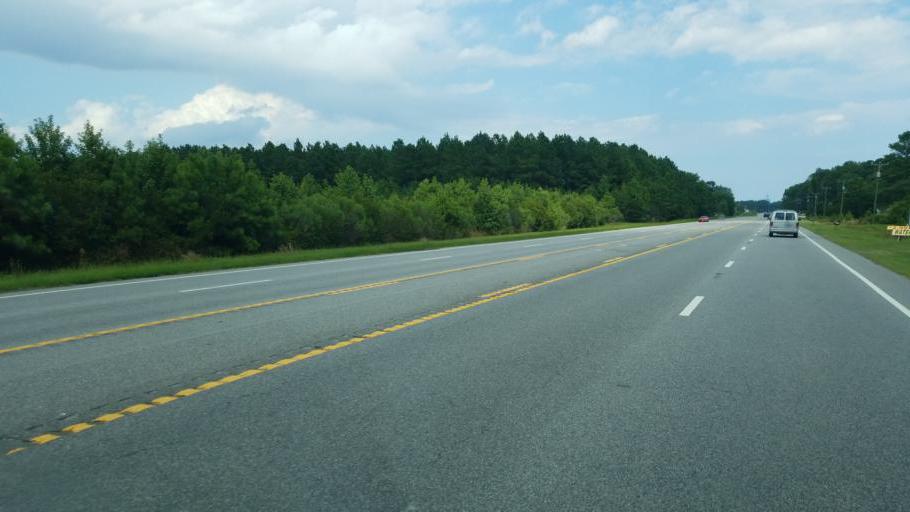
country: US
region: North Carolina
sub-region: Currituck County
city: Currituck
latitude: 36.4545
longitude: -76.0500
